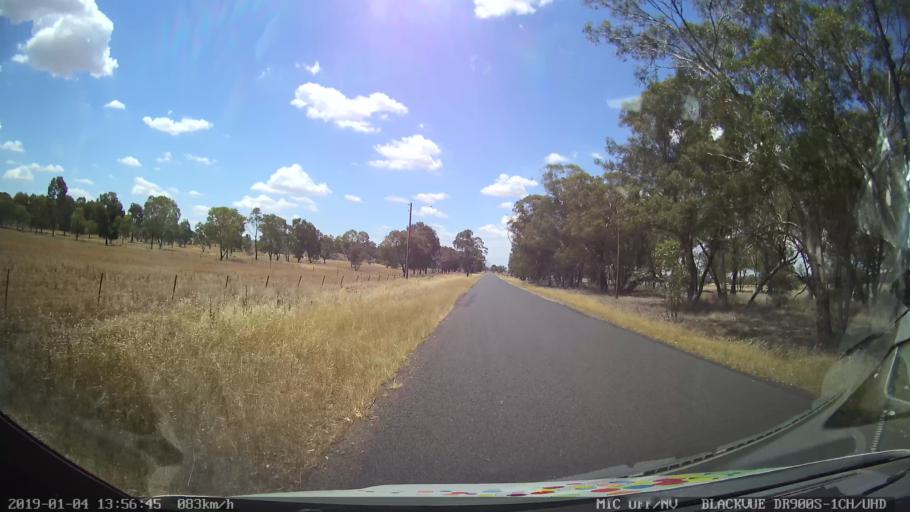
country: AU
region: New South Wales
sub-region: Dubbo Municipality
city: Dubbo
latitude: -32.3477
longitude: 148.5965
